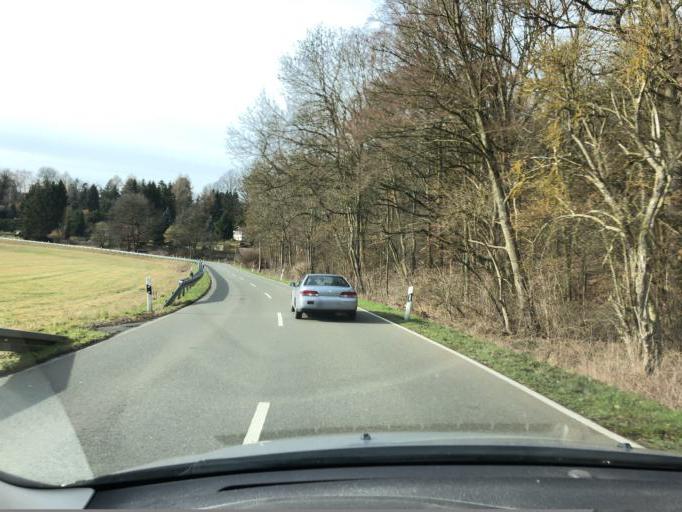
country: DE
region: Saxony-Anhalt
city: Bad Bibra
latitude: 51.2205
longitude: 11.5944
